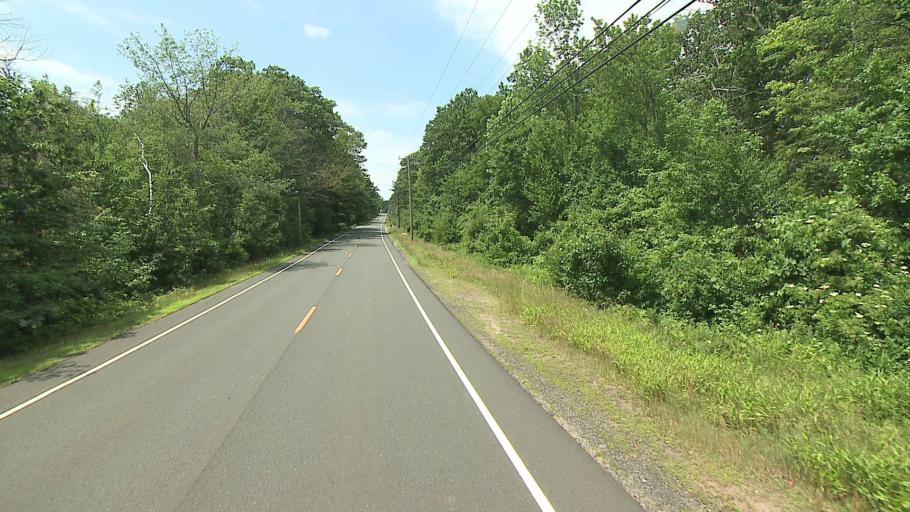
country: US
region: Connecticut
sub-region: Hartford County
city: North Granby
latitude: 41.9953
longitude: -72.8906
